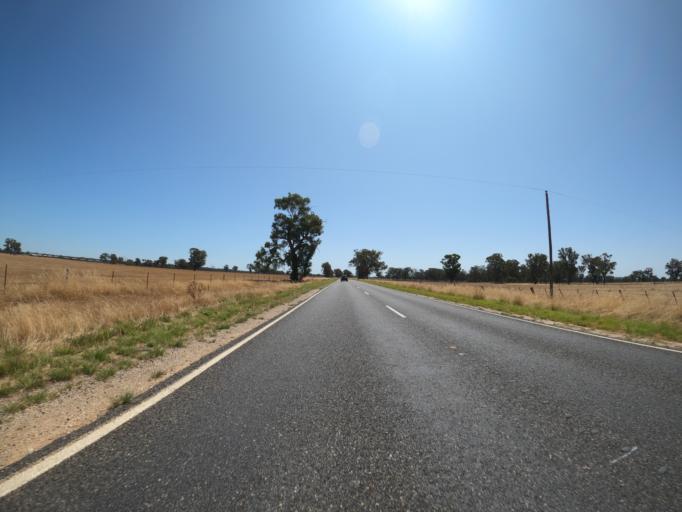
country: AU
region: New South Wales
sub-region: Corowa Shire
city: Corowa
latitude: -36.0742
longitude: 146.2408
